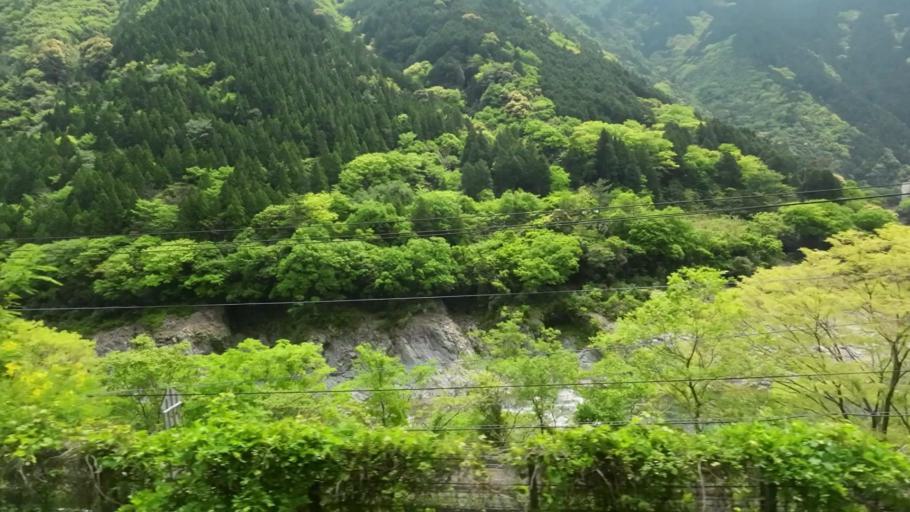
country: JP
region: Tokushima
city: Ikedacho
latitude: 33.9182
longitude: 133.7566
